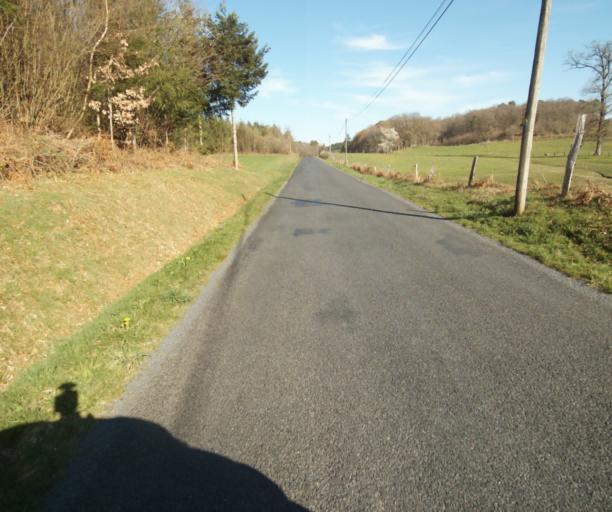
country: FR
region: Limousin
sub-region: Departement de la Correze
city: Correze
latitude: 45.2797
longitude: 1.8798
